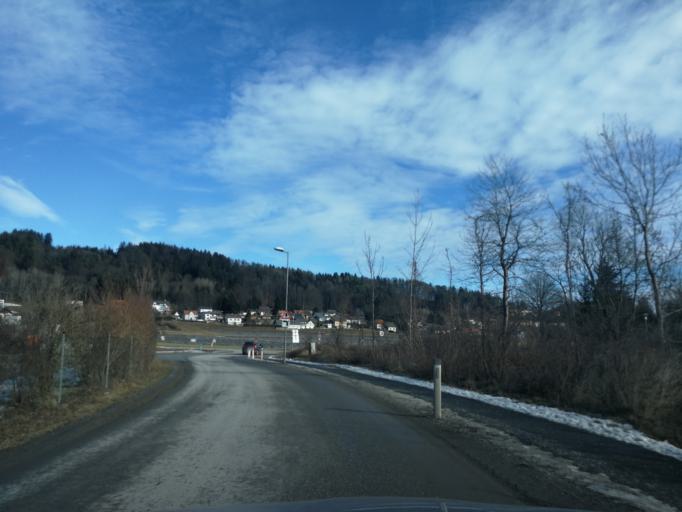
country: AT
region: Styria
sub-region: Politischer Bezirk Weiz
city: Ungerdorf
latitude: 47.1022
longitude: 15.6694
